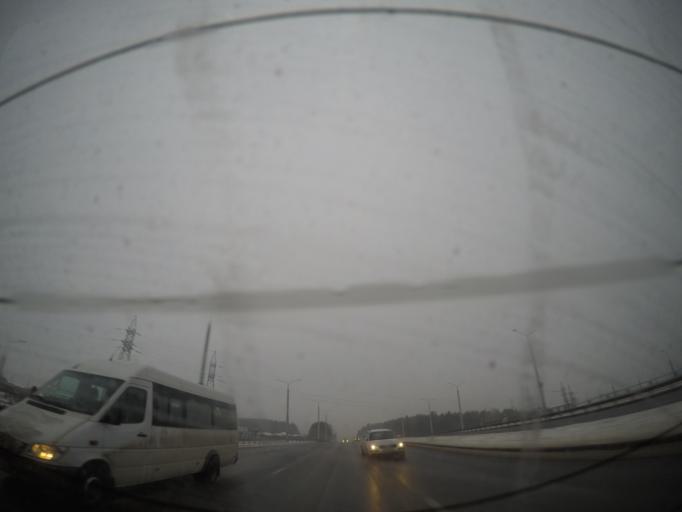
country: BY
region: Grodnenskaya
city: Hrodna
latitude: 53.6356
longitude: 23.8104
